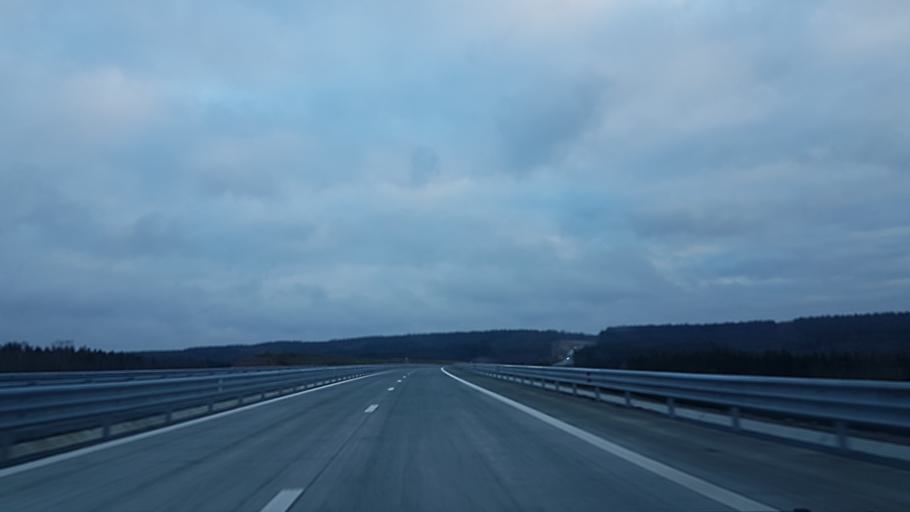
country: BE
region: Wallonia
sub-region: Province de Namur
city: Couvin
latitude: 50.0155
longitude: 4.5318
